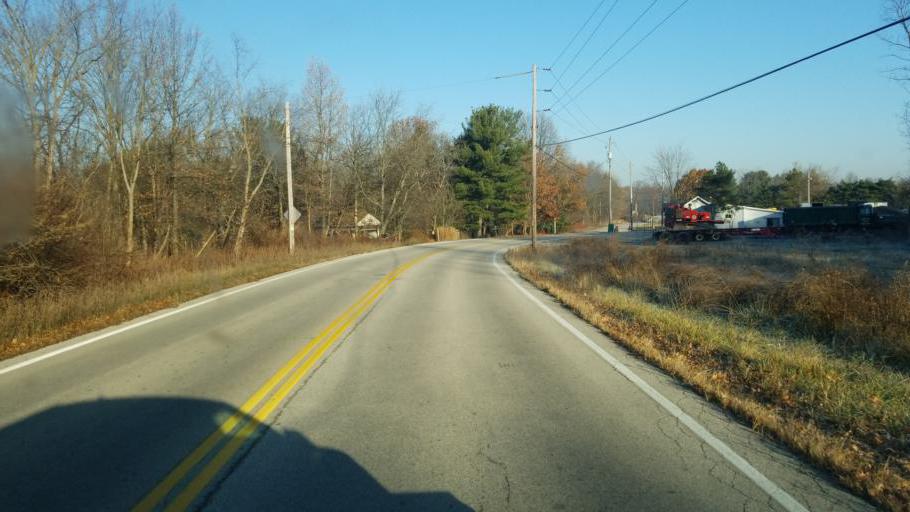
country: US
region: Ohio
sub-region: Summit County
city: Silver Lake
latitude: 41.1989
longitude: -81.4721
